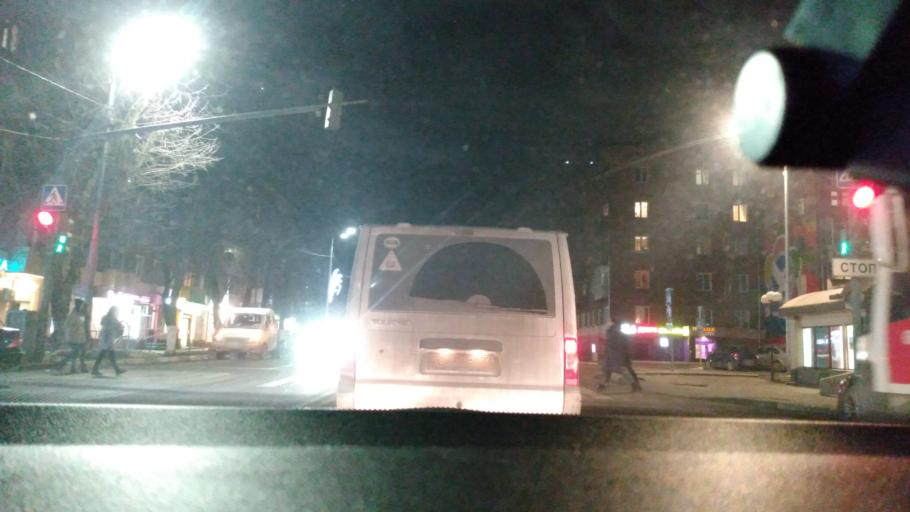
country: RU
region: Moskovskaya
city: Balashikha
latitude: 55.7998
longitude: 37.9346
